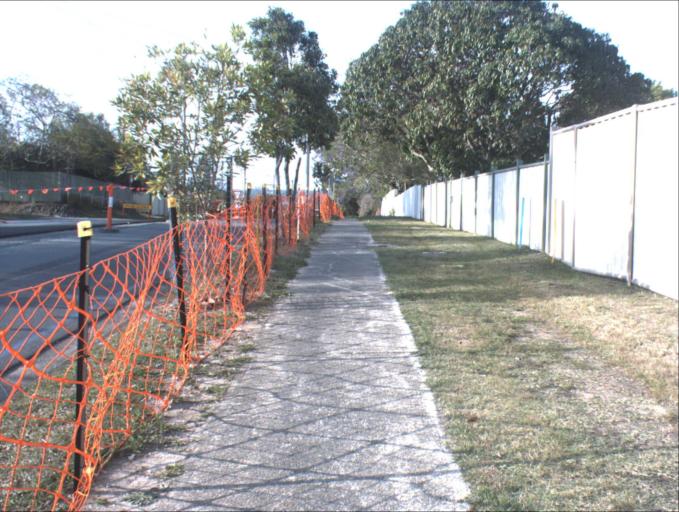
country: AU
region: Queensland
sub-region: Logan
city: Woodridge
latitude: -27.6276
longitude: 153.1098
